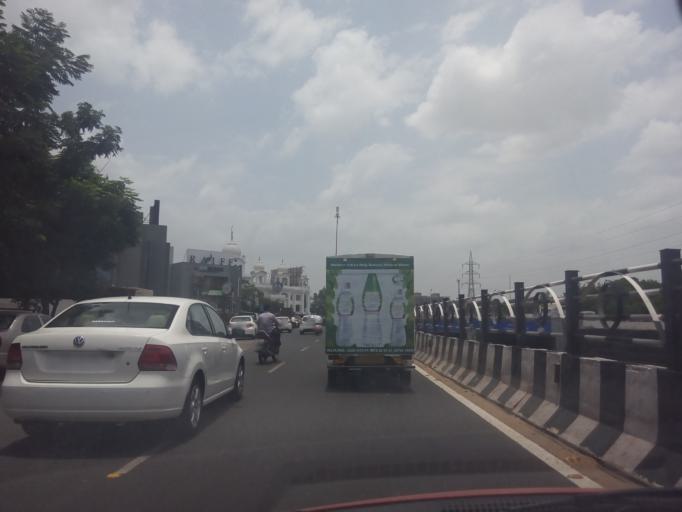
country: IN
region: Gujarat
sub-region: Ahmadabad
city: Sarkhej
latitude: 23.0454
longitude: 72.5150
